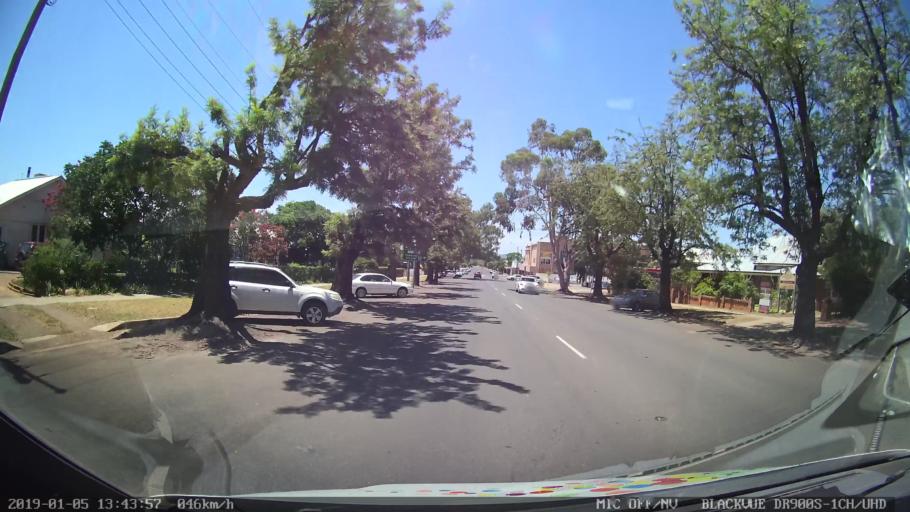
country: AU
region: New South Wales
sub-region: Gunnedah
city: Gunnedah
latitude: -30.9807
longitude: 150.2552
